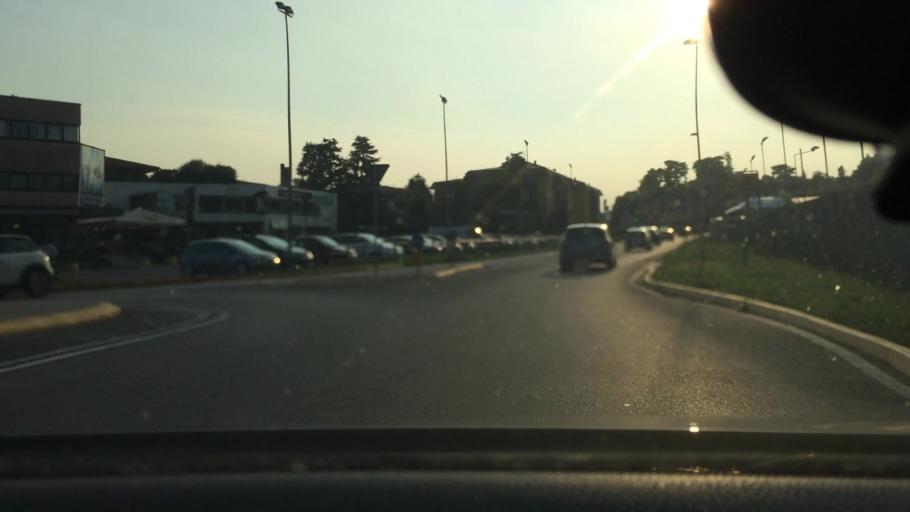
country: IT
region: Lombardy
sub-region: Provincia di Bergamo
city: Curno
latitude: 45.6930
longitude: 9.6148
